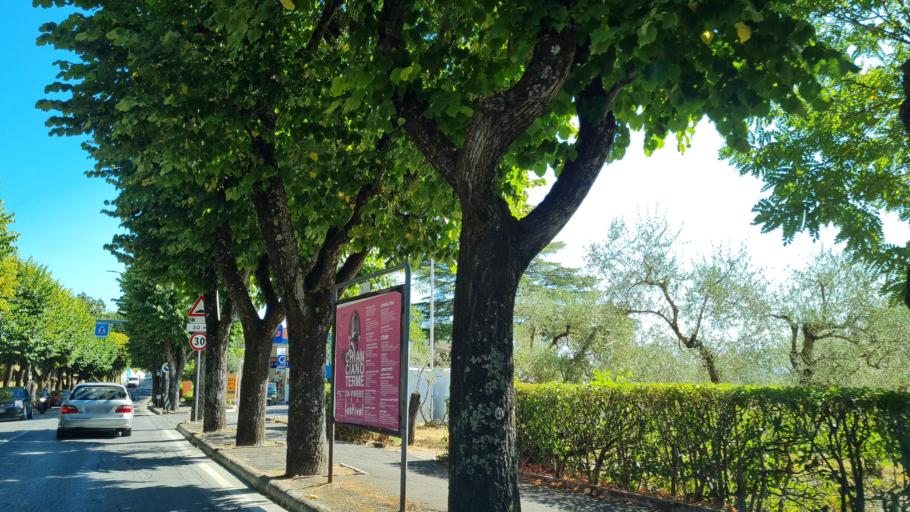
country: IT
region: Tuscany
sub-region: Provincia di Siena
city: Chianciano Terme
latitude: 43.0517
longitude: 11.8210
